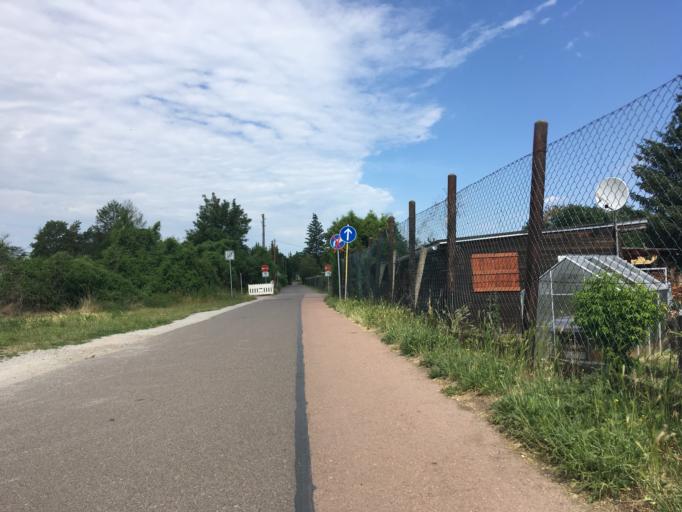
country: DE
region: Saxony-Anhalt
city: Bernburg
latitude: 51.7883
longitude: 11.7596
